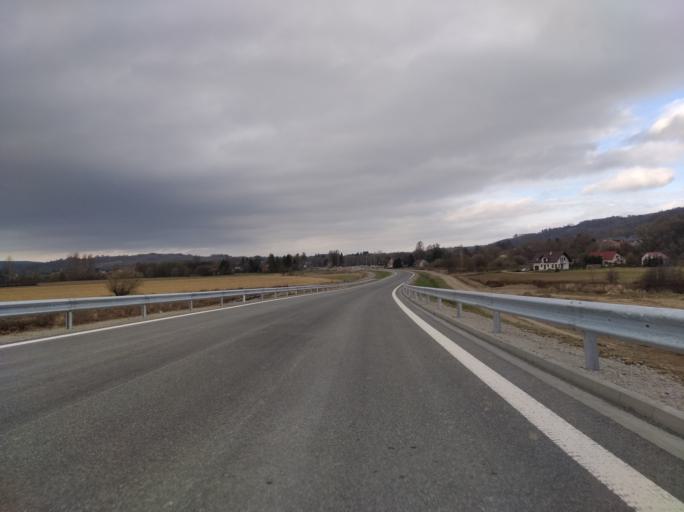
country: PL
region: Subcarpathian Voivodeship
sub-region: Powiat strzyzowski
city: Strzyzow
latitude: 49.8699
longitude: 21.7680
